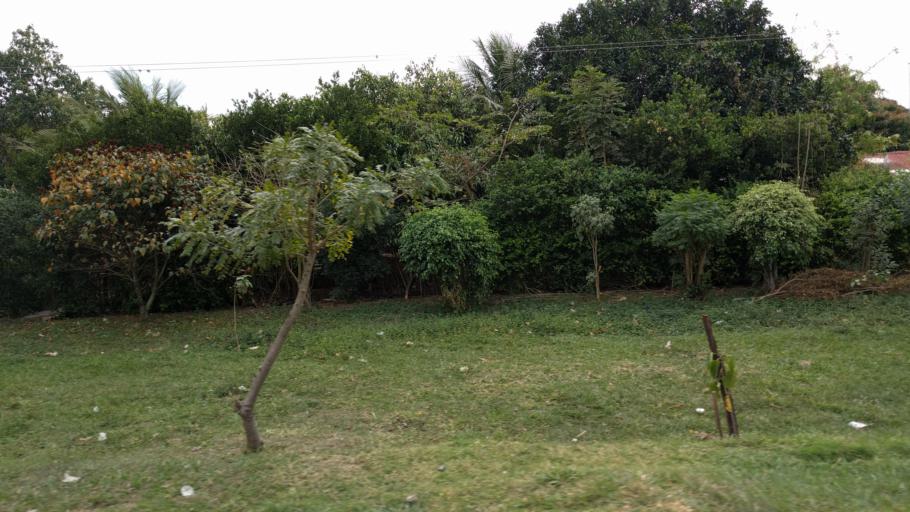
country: BO
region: Santa Cruz
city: Jorochito
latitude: -18.0454
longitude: -63.4178
